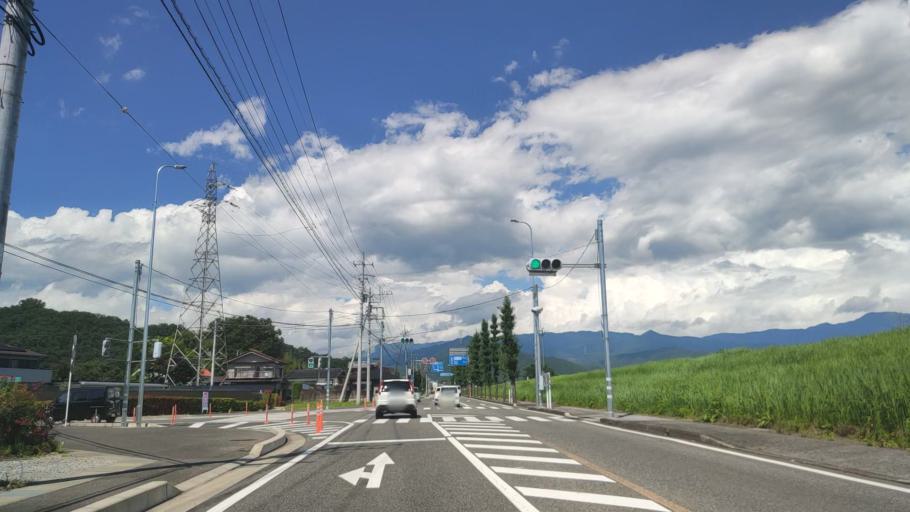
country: JP
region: Yamanashi
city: Enzan
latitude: 35.7012
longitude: 138.6908
